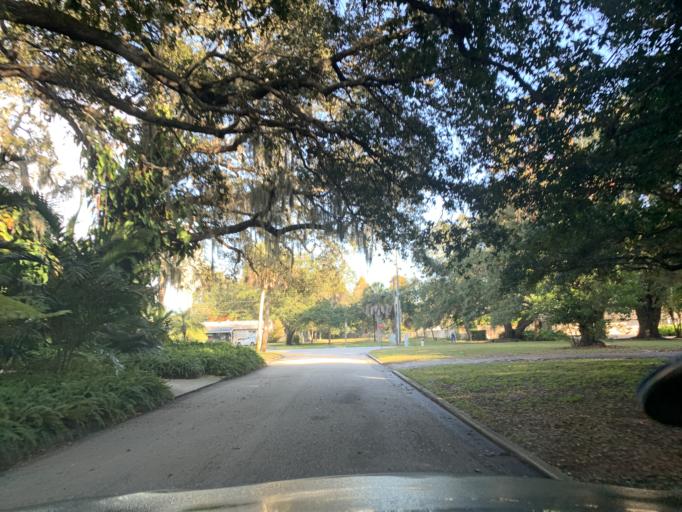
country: US
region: Florida
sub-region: Pinellas County
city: Bay Pines
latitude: 27.8059
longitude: -82.7517
